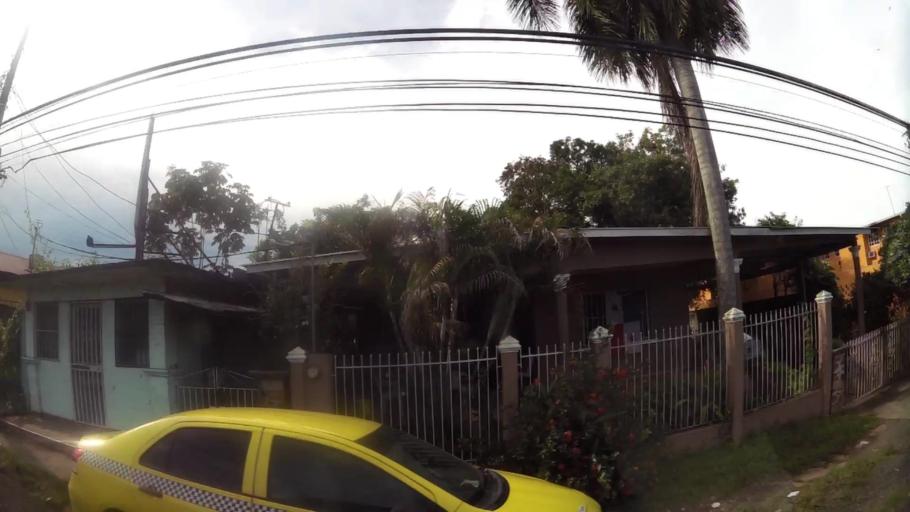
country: PA
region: Panama
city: La Chorrera
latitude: 8.8829
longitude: -79.7764
